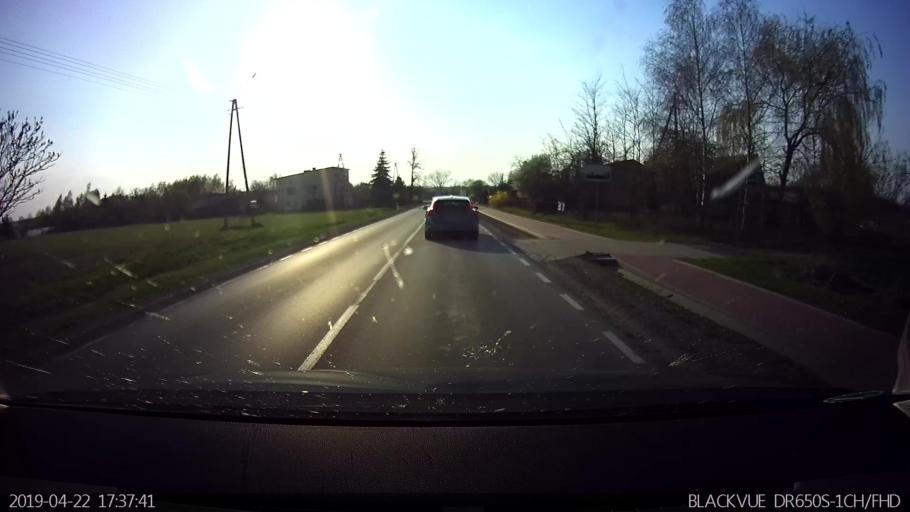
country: PL
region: Masovian Voivodeship
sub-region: Powiat sokolowski
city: Sokolow Podlaski
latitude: 52.4102
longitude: 22.1704
